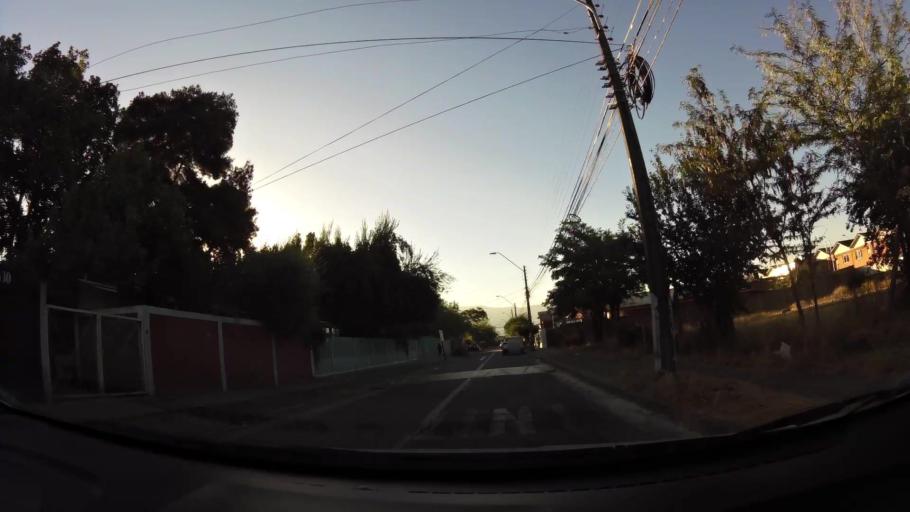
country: CL
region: O'Higgins
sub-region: Provincia de Cachapoal
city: Rancagua
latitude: -34.1719
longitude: -70.7586
